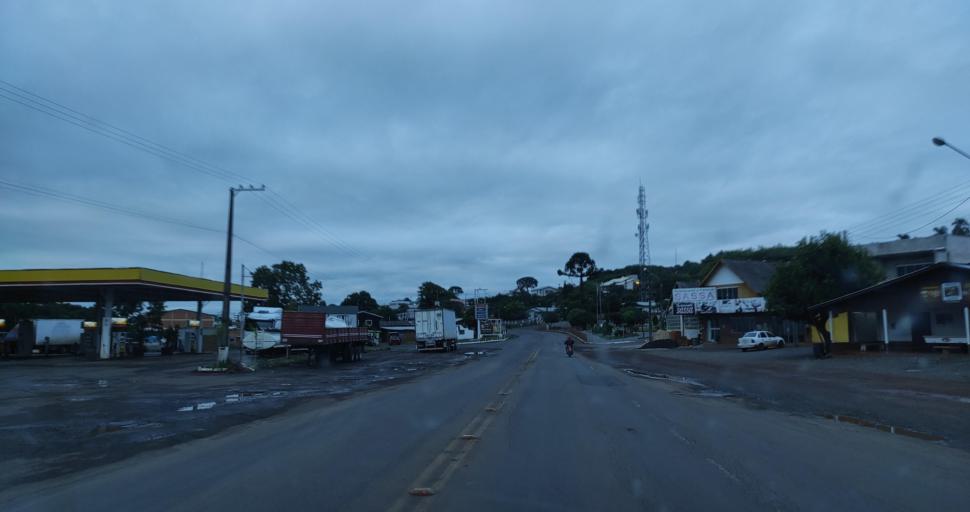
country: BR
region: Santa Catarina
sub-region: Xanxere
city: Xanxere
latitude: -26.7354
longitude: -52.3913
